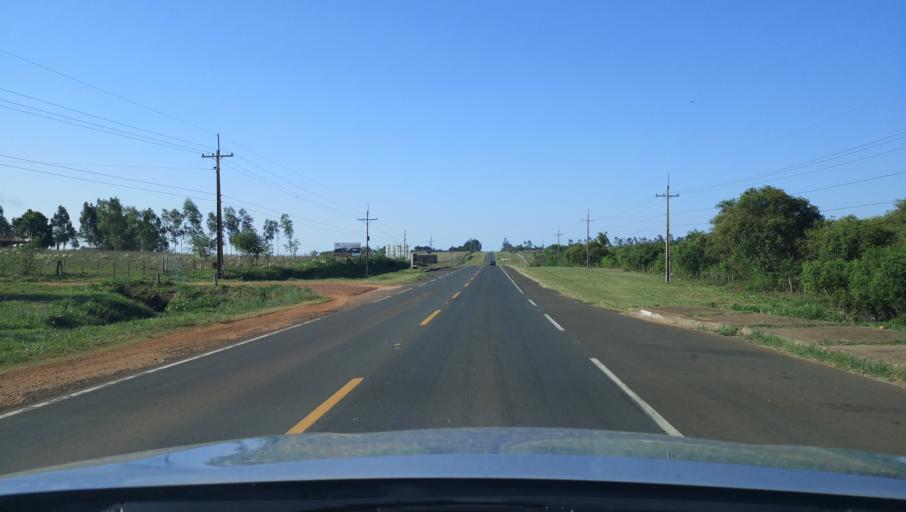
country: PY
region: Misiones
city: Santa Maria
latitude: -26.8335
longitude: -57.0326
